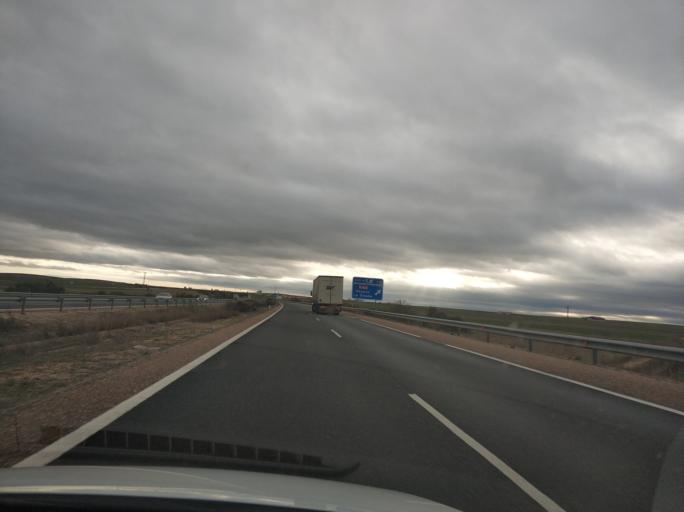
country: ES
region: Castille and Leon
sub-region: Provincia de Salamanca
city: Pajares de la Laguna
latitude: 41.1012
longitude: -5.4978
